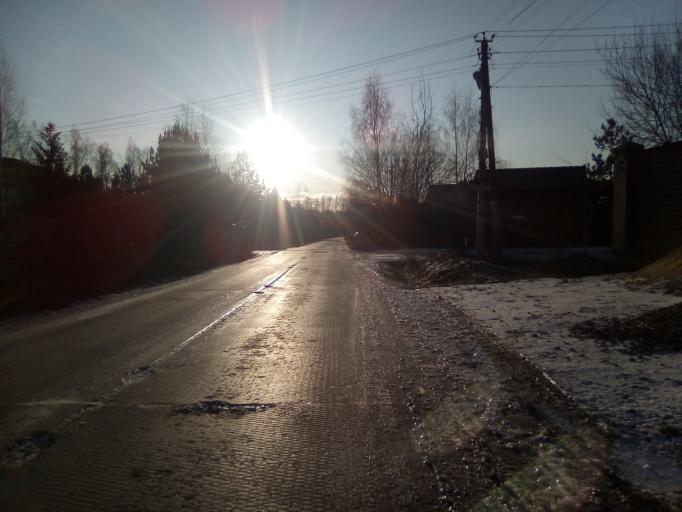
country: RU
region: Moskovskaya
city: Zhavoronki
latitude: 55.6451
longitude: 37.1489
